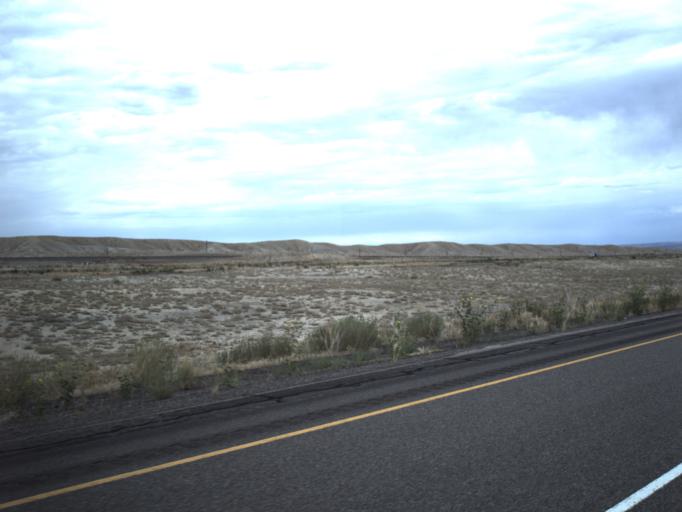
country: US
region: Utah
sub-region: Grand County
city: Moab
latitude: 38.9343
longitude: -109.4586
